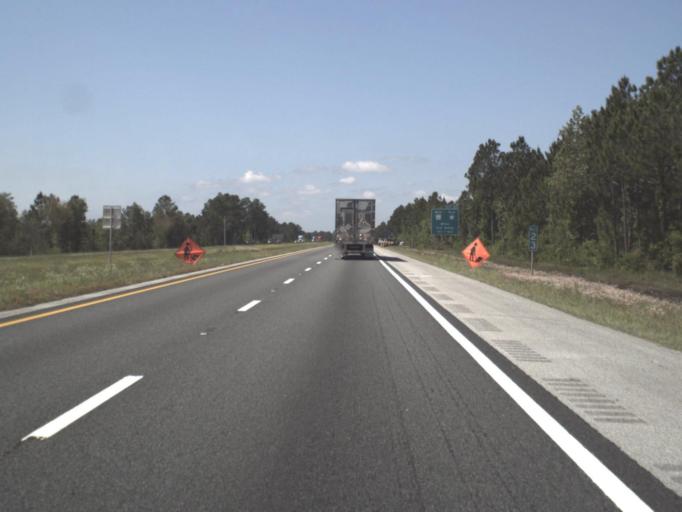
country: US
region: Florida
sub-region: Santa Rosa County
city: Bagdad
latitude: 30.5421
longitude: -87.0678
